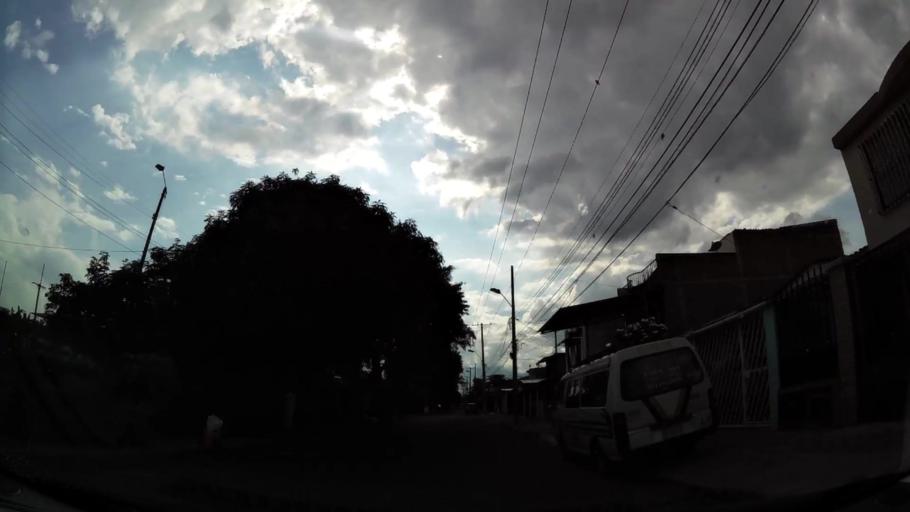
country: CO
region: Valle del Cauca
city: Cali
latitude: 3.4700
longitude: -76.4874
